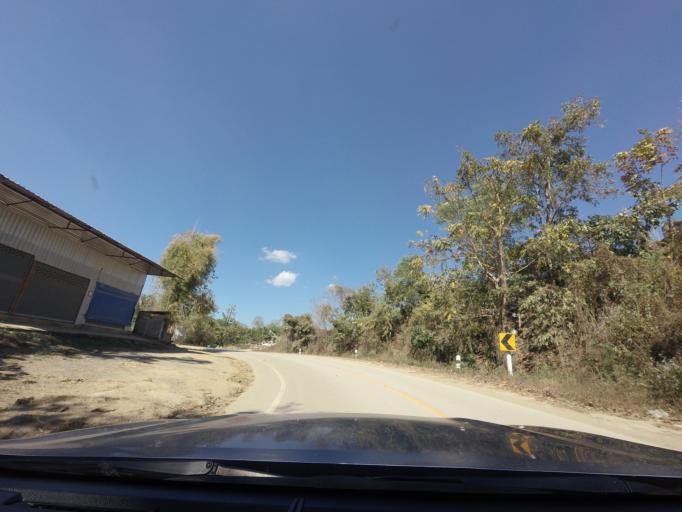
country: TH
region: Lampang
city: Chae Hom
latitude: 18.6153
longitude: 99.6239
